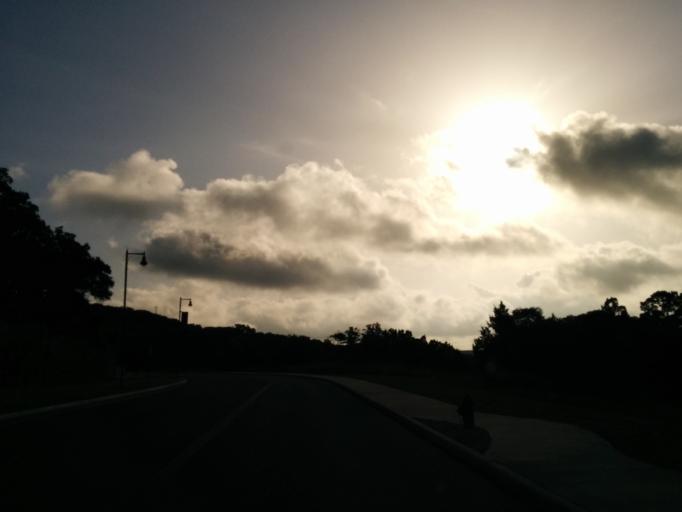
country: US
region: Texas
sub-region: Bexar County
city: Cross Mountain
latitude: 29.6122
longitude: -98.6099
